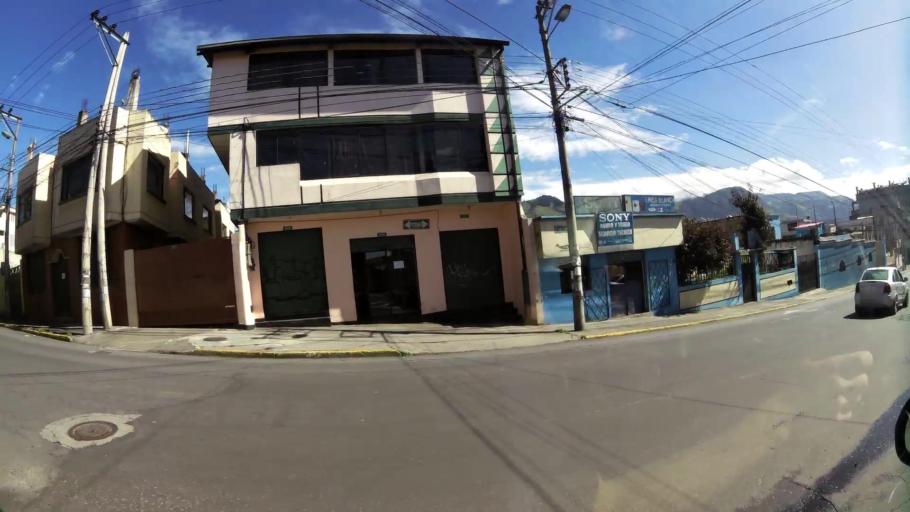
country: EC
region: Pichincha
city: Quito
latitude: -0.2856
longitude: -78.5602
